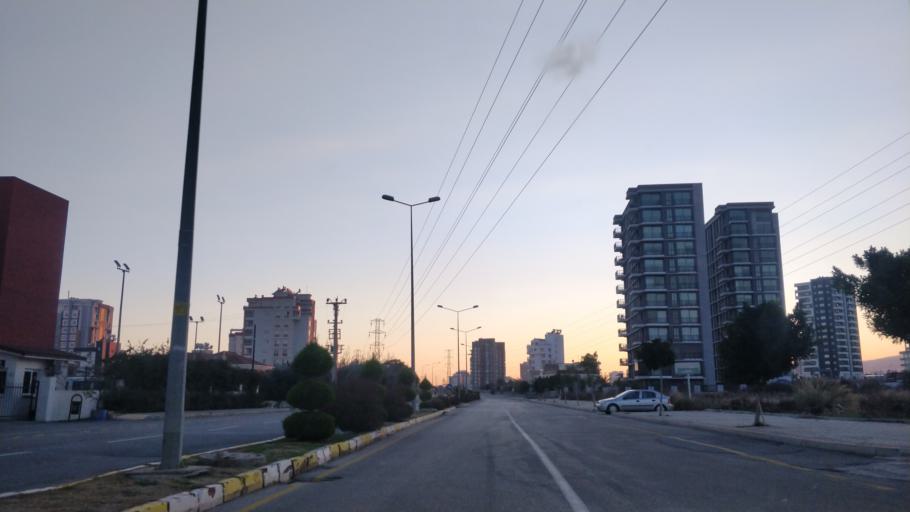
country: TR
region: Mersin
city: Mercin
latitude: 36.8053
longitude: 34.5729
